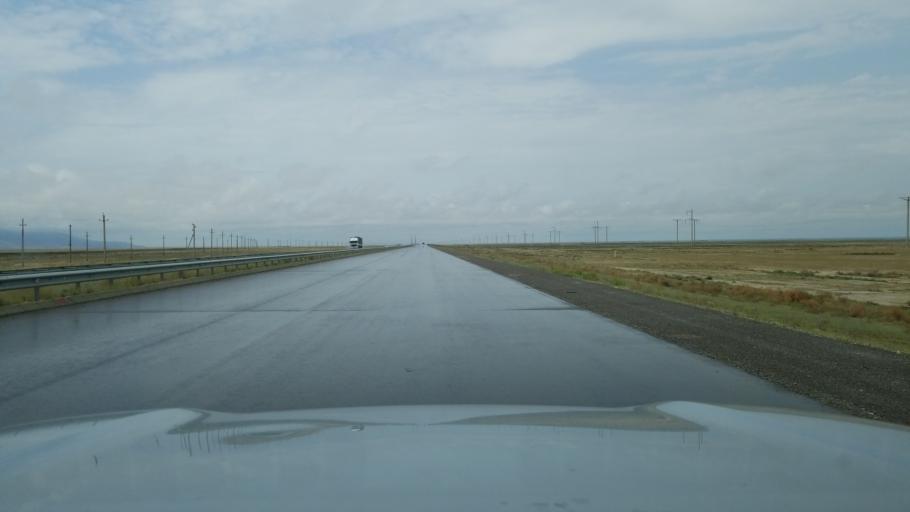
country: TM
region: Balkan
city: Gazanjyk
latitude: 39.1617
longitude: 55.8365
